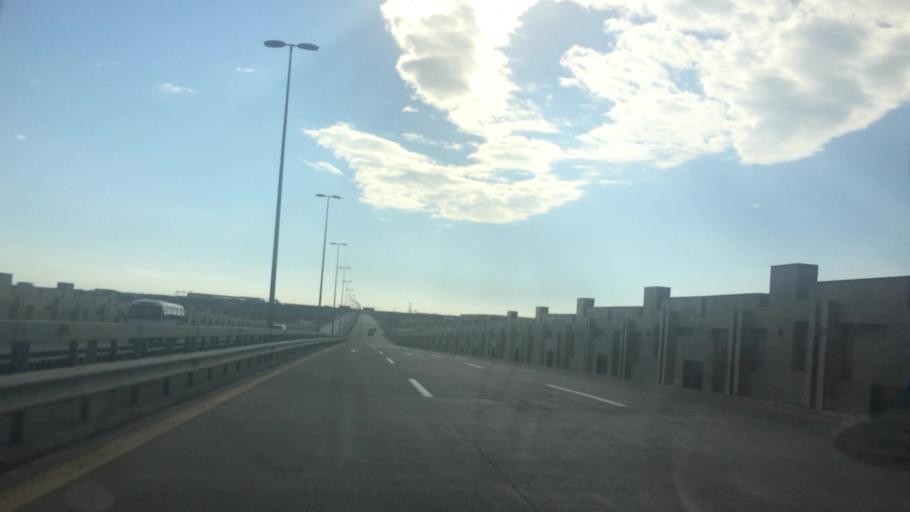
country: AZ
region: Baki
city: Hovsan
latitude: 40.3904
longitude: 50.0715
